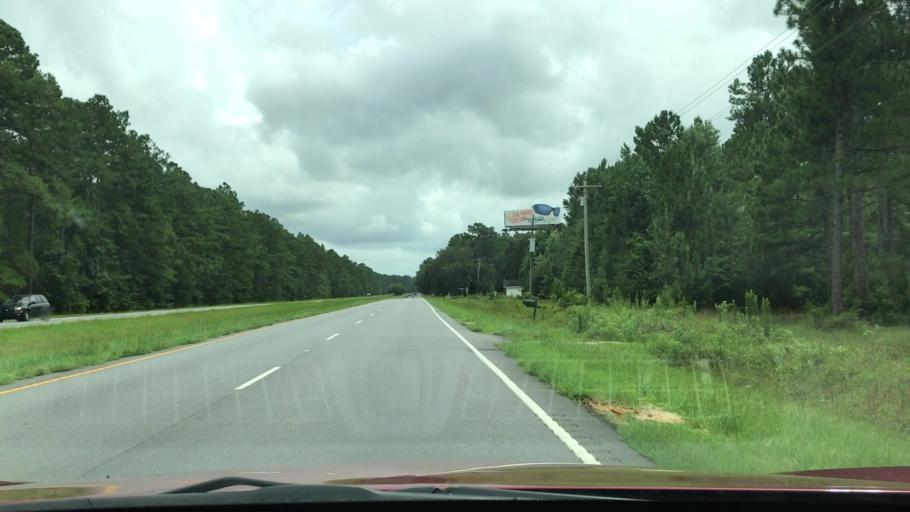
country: US
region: South Carolina
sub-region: Georgetown County
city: Georgetown
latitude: 33.2424
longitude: -79.3757
